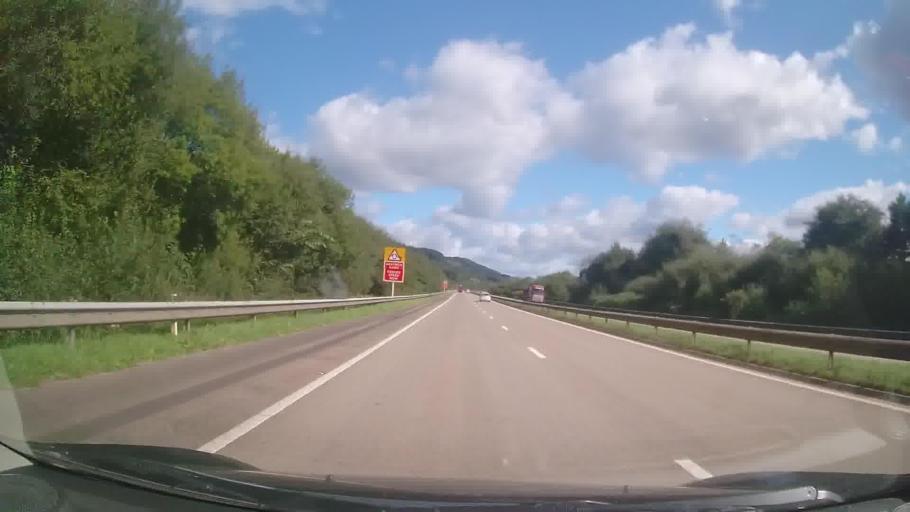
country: GB
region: Wales
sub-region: Neath Port Talbot
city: Resolven
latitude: 51.7082
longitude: -3.7066
